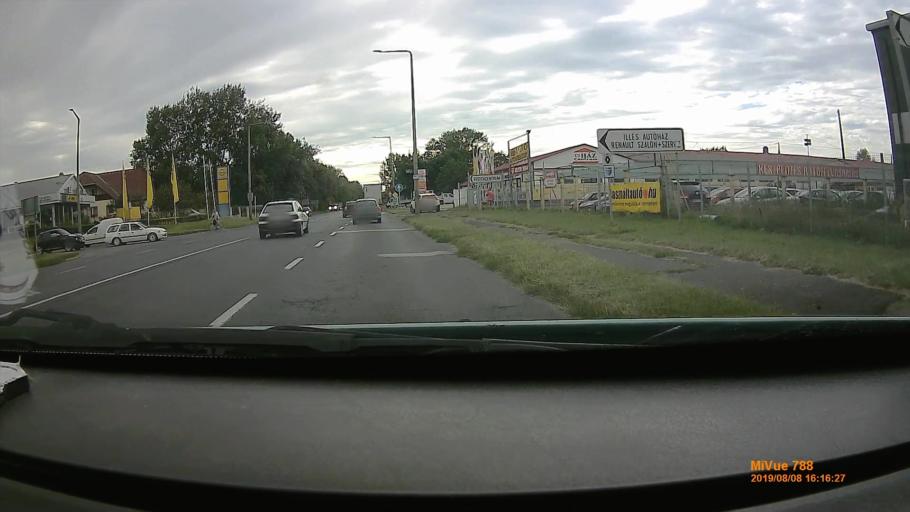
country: HU
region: Szabolcs-Szatmar-Bereg
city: Mateszalka
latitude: 47.9615
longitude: 22.3043
